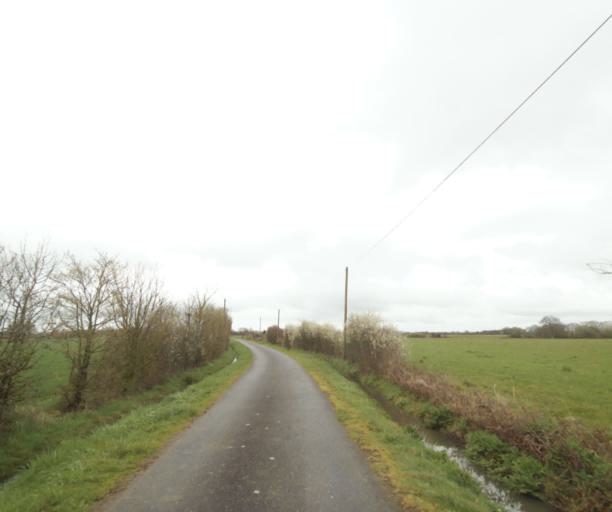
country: FR
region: Pays de la Loire
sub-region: Departement de la Loire-Atlantique
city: Bouvron
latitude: 47.4530
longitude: -1.8940
